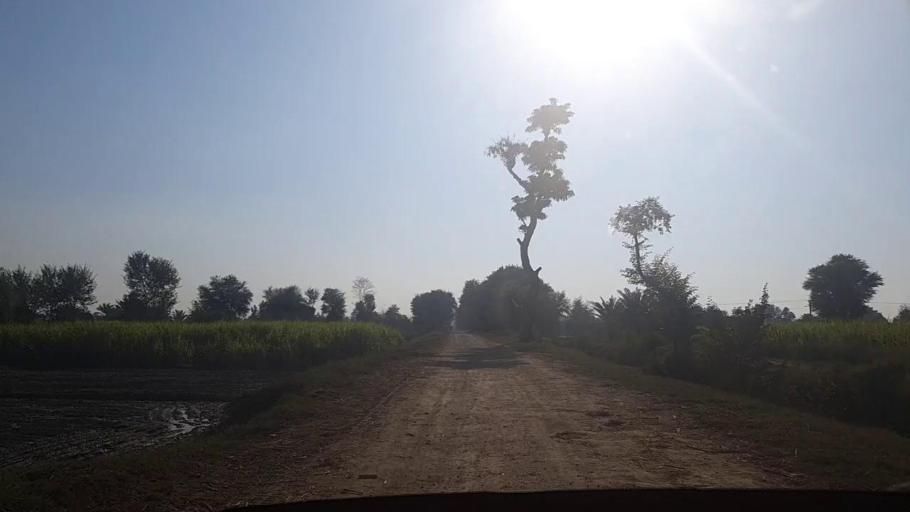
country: PK
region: Sindh
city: Gambat
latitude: 27.3772
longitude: 68.4675
